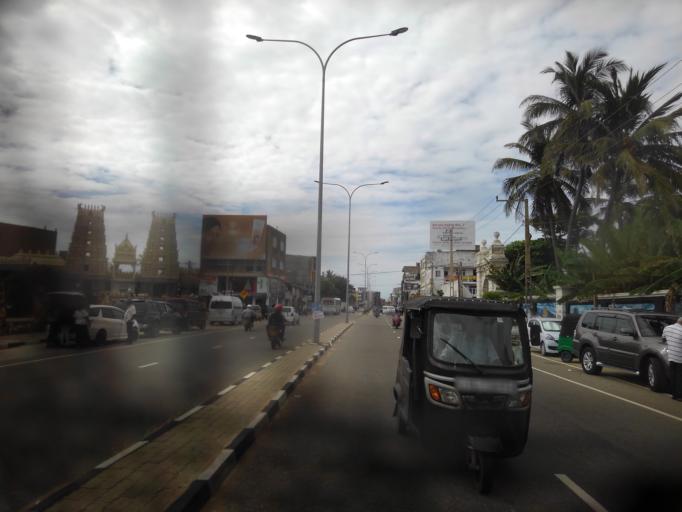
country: LK
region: Southern
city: Galle
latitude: 6.0336
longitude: 80.2134
